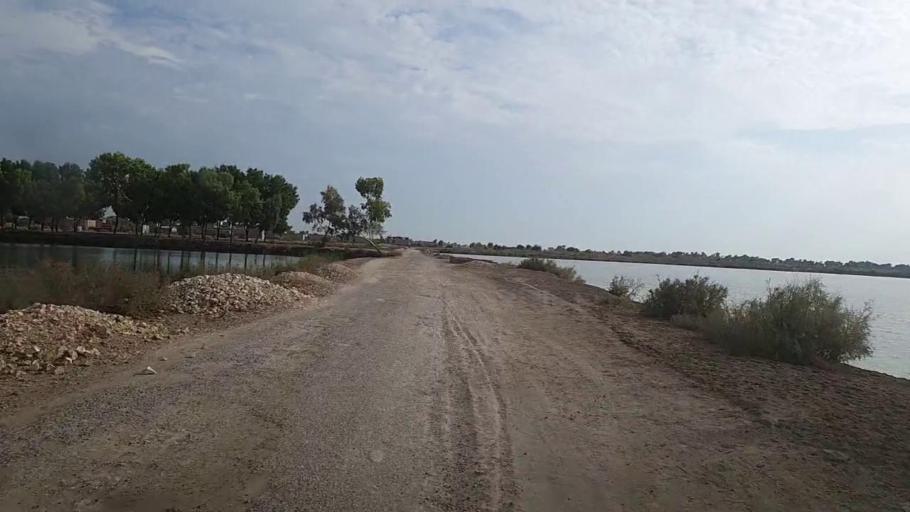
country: PK
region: Sindh
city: Thul
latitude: 28.2719
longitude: 68.8540
